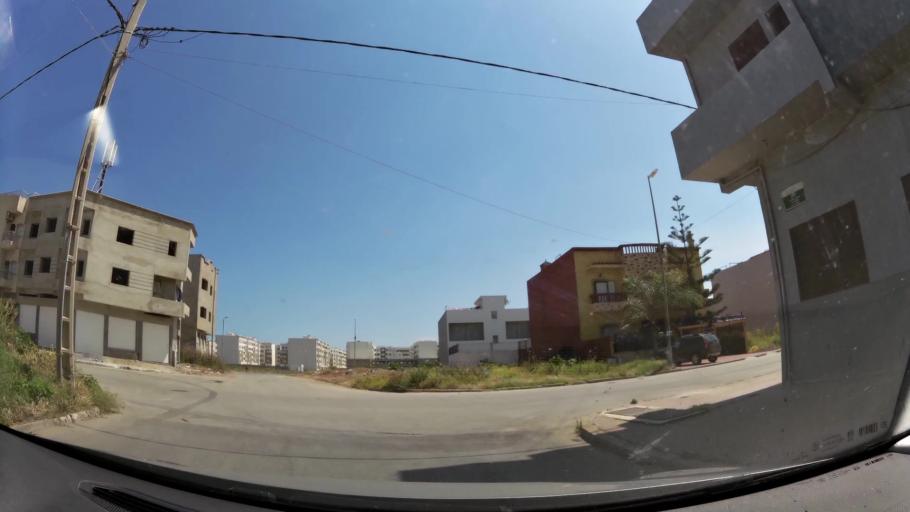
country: MA
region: Rabat-Sale-Zemmour-Zaer
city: Sale
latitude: 34.0762
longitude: -6.7843
